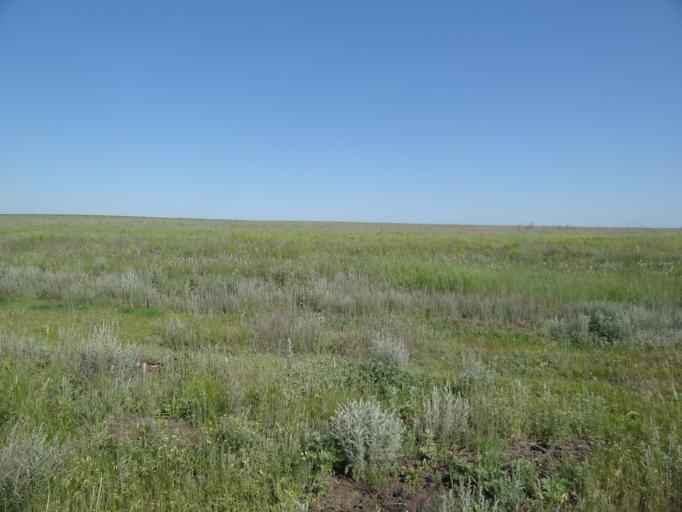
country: RU
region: Saratov
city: Krasnoarmeysk
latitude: 51.2591
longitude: 45.5925
